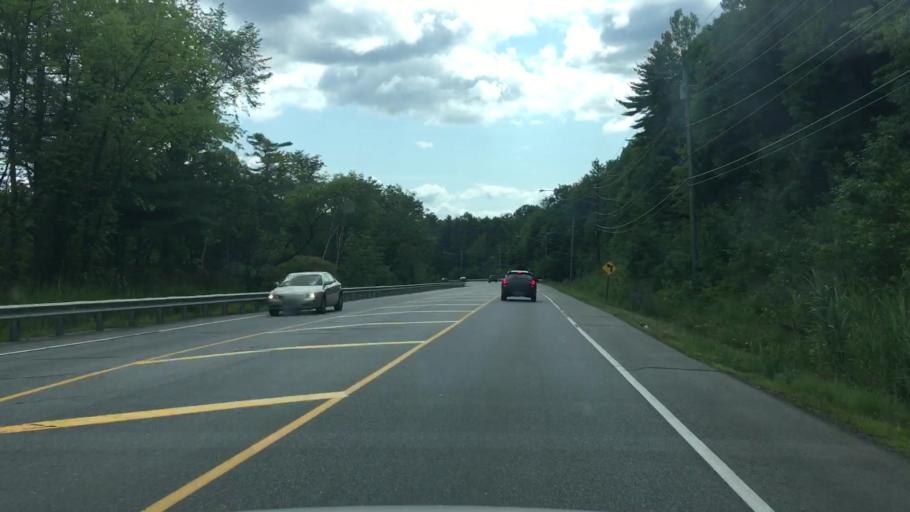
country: US
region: Maine
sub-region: Kennebec County
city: Augusta
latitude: 44.3355
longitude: -69.7929
